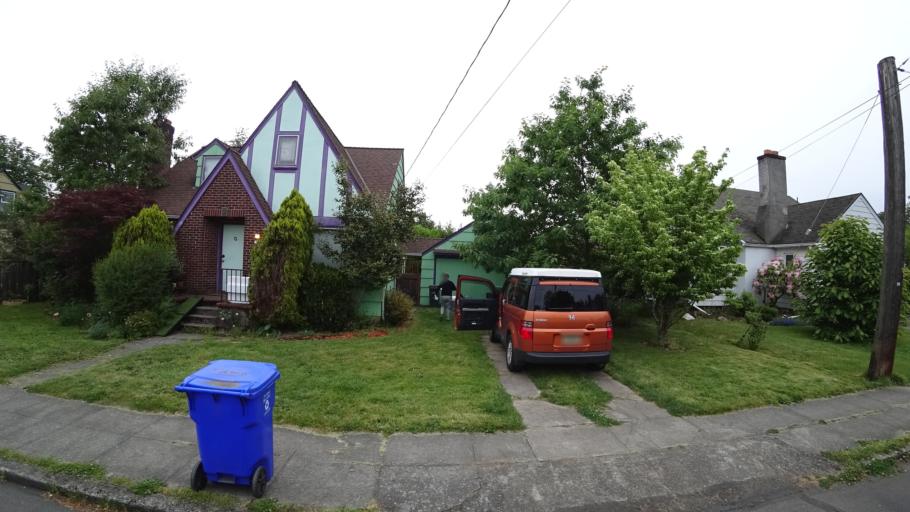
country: US
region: Oregon
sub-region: Multnomah County
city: Portland
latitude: 45.5598
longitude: -122.6255
